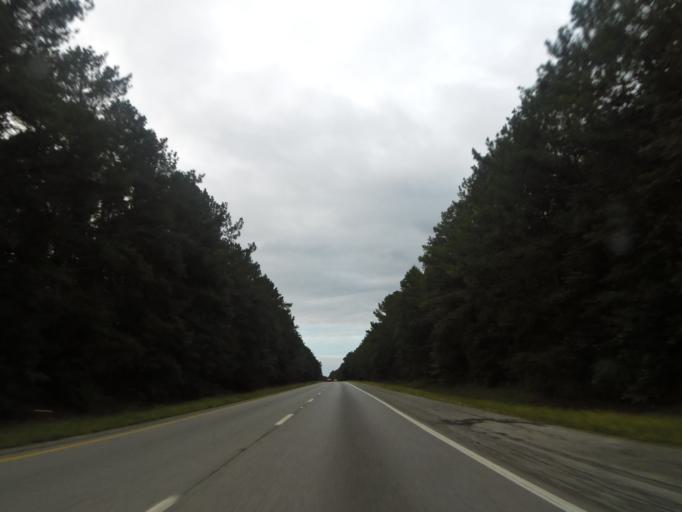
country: US
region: Alabama
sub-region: Saint Clair County
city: Ashville
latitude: 33.8349
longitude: -86.3292
